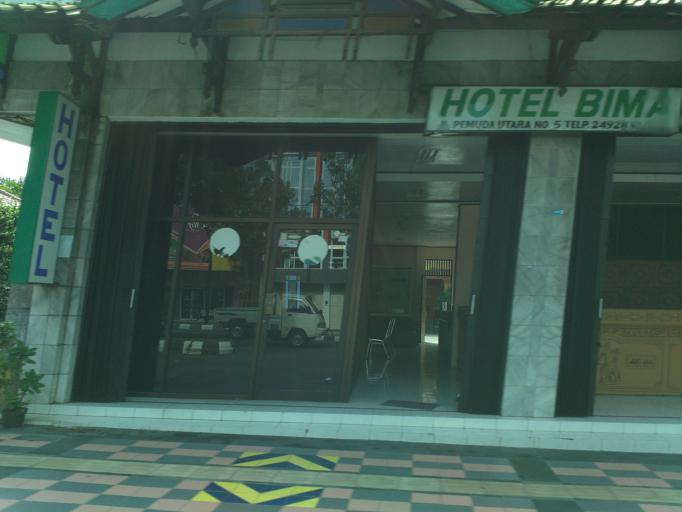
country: ID
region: Central Java
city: Klaten
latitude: -7.6965
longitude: 110.6082
